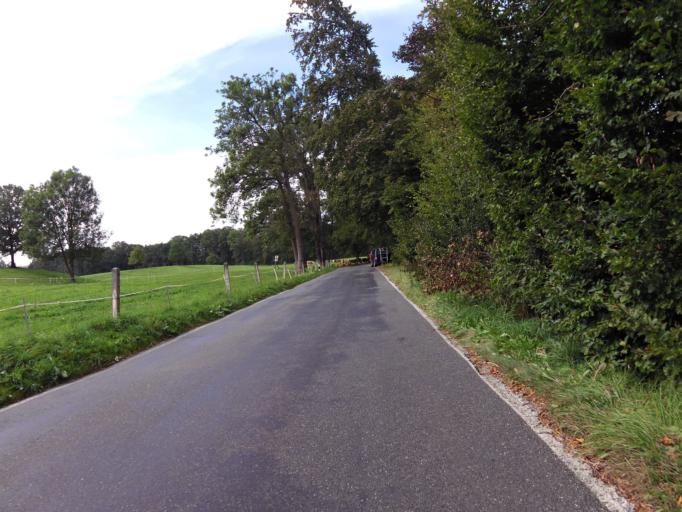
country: DE
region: Bavaria
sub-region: Upper Bavaria
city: Seeshaupt
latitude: 47.8295
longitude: 11.2930
